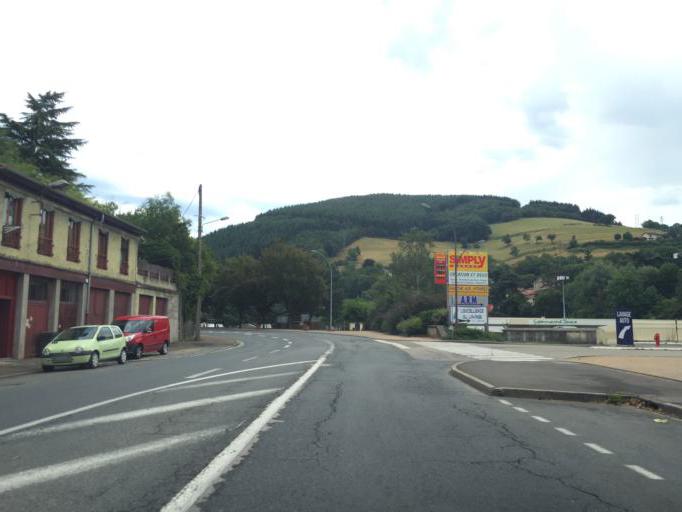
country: FR
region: Rhone-Alpes
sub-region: Departement du Rhone
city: Tarare
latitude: 45.8912
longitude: 4.4429
